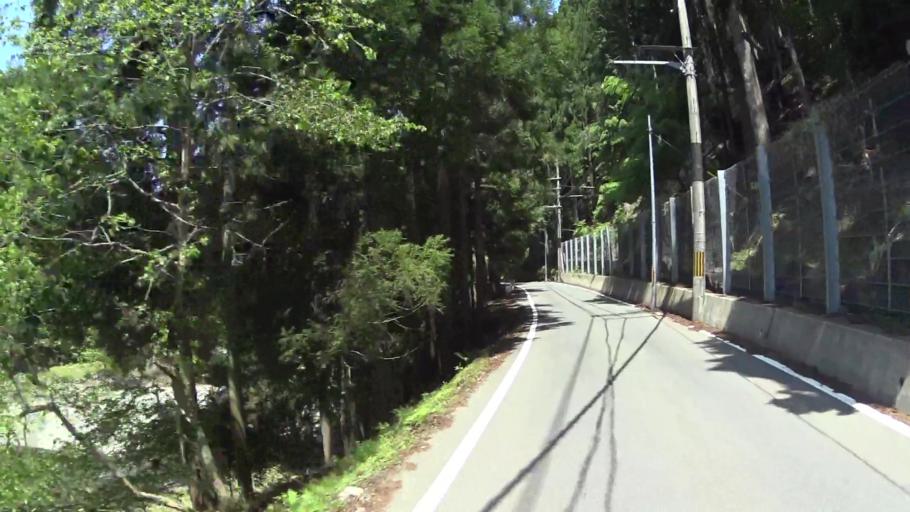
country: JP
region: Shiga Prefecture
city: Kitahama
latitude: 35.2057
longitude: 135.7589
